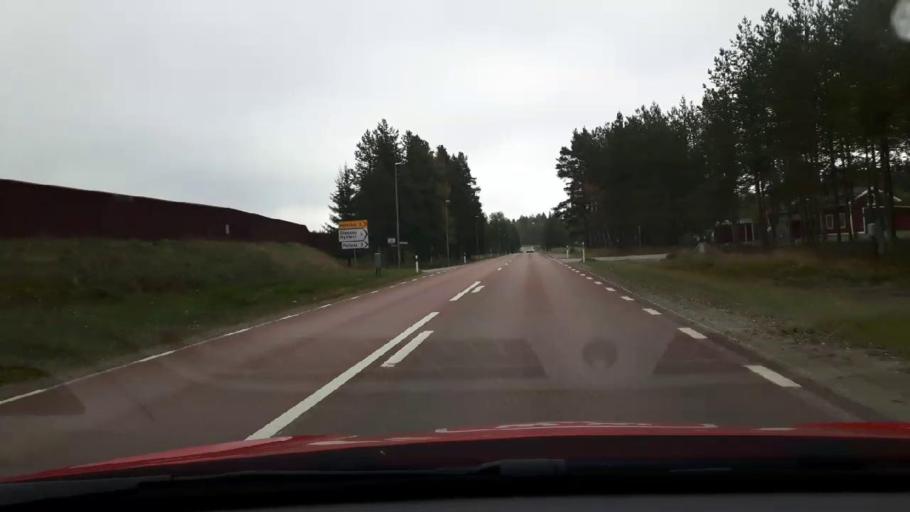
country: SE
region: Gaevleborg
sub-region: Ljusdals Kommun
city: Farila
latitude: 61.8026
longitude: 15.7886
